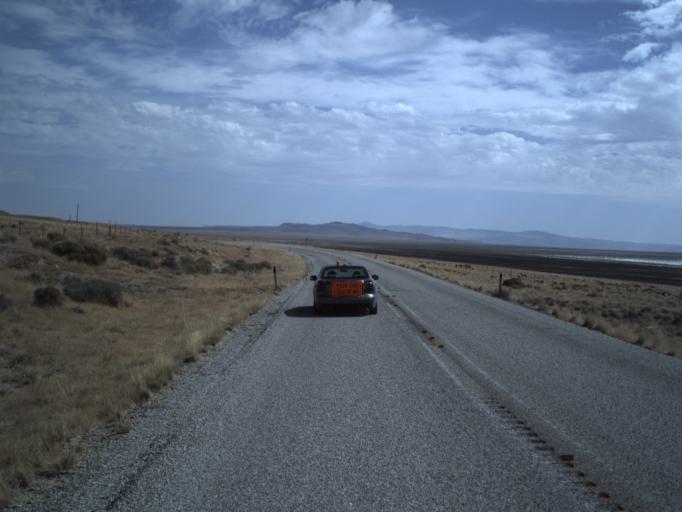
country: US
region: Utah
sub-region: Tooele County
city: Wendover
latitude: 41.4418
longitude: -113.6961
